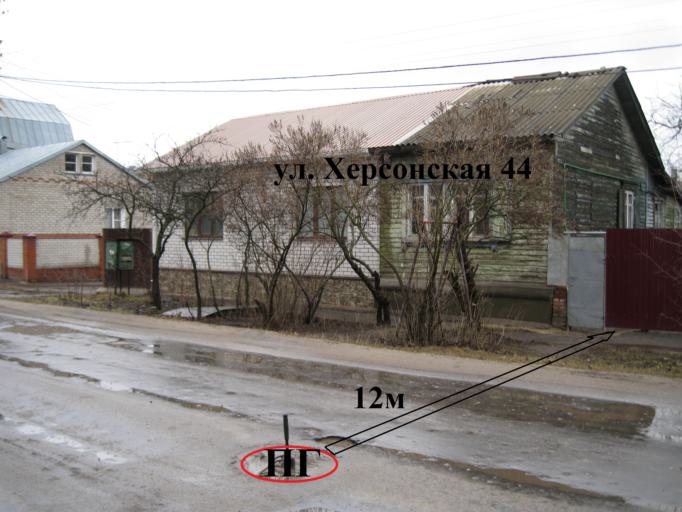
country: RU
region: Voronezj
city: Voronezh
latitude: 51.6304
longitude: 39.1765
